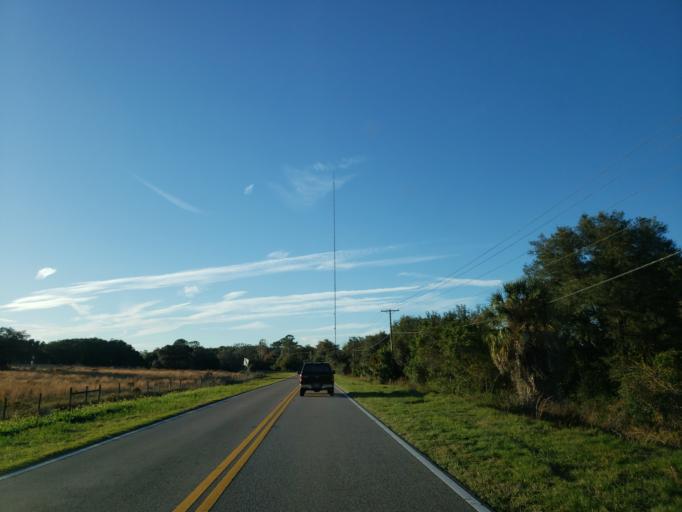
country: US
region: Florida
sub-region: Hillsborough County
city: Boyette
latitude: 27.8240
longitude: -82.2556
